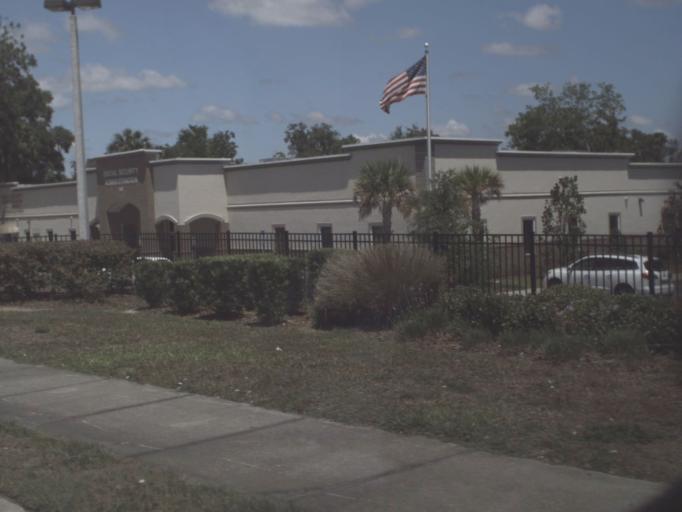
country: US
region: Florida
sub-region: Marion County
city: Ocala
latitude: 29.1871
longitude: -82.1267
